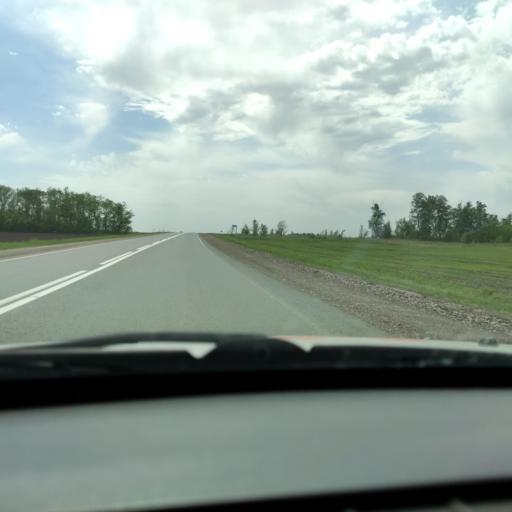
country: RU
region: Samara
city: Novyy Buyan
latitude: 53.6791
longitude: 50.2170
